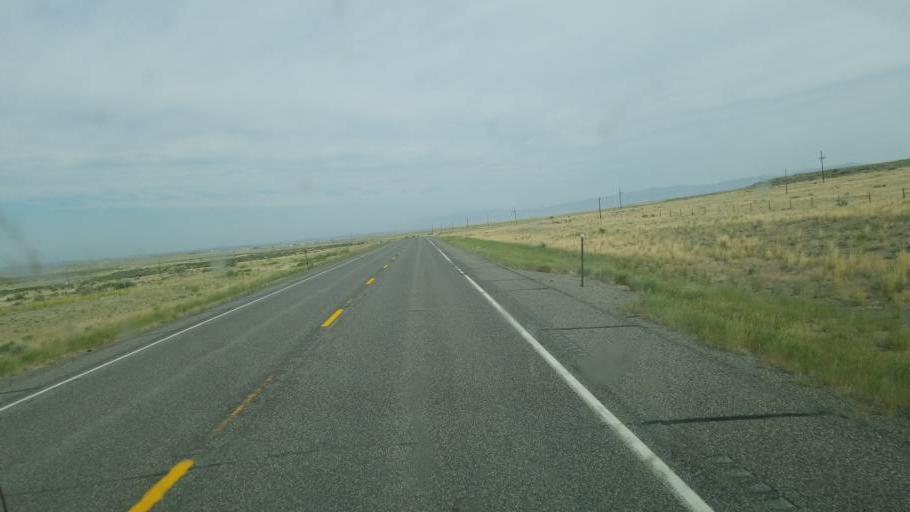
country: US
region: Wyoming
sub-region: Fremont County
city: Riverton
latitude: 43.2287
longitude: -108.0571
